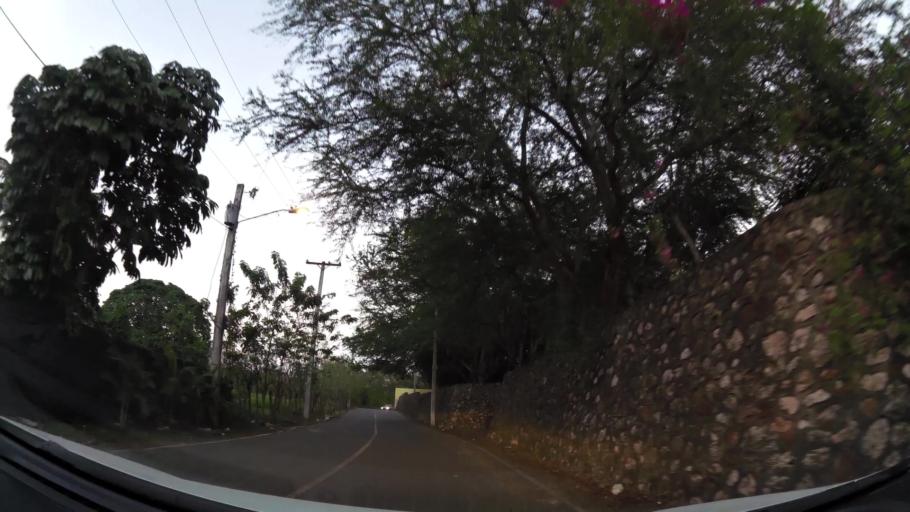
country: DO
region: Nacional
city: La Agustina
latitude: 18.5440
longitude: -69.9504
